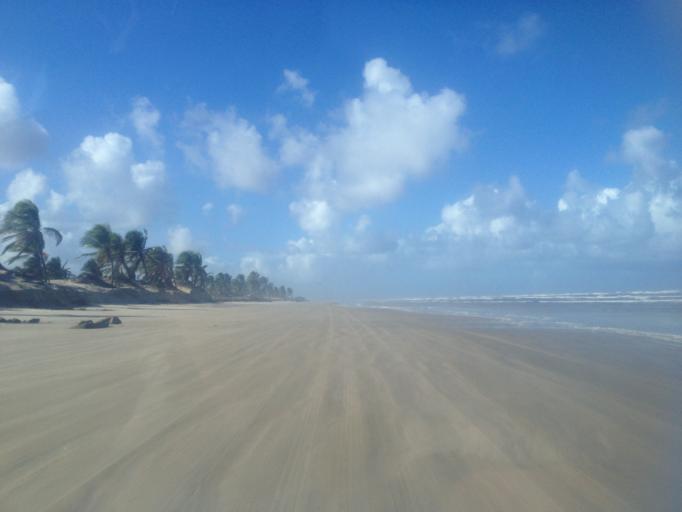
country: BR
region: Sergipe
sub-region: Indiaroba
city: Indiaroba
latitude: -11.4714
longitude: -37.3581
